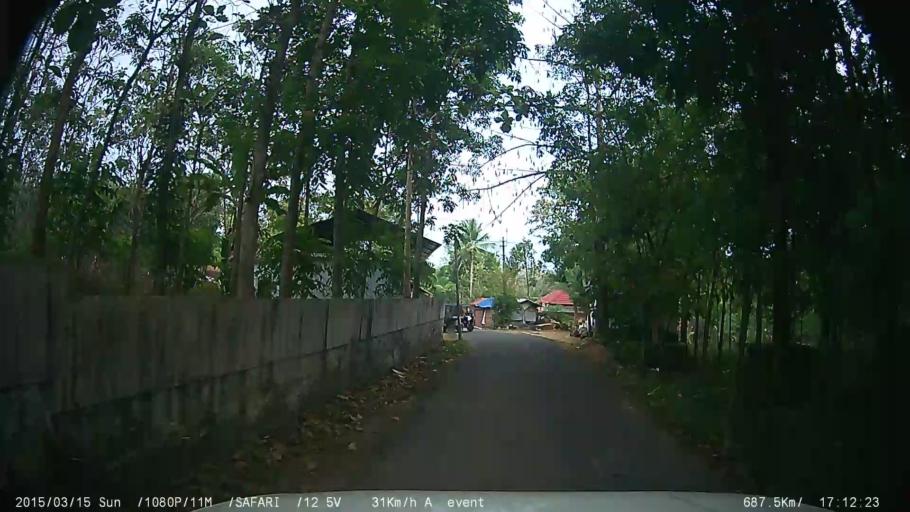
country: IN
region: Kerala
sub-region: Kottayam
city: Palackattumala
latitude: 9.8559
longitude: 76.6804
